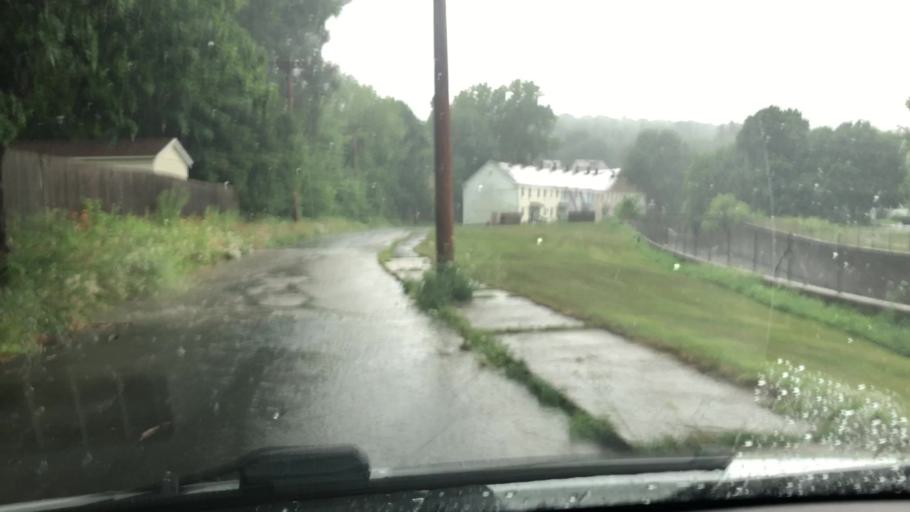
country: US
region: Massachusetts
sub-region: Berkshire County
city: Adams
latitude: 42.6240
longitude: -73.1155
